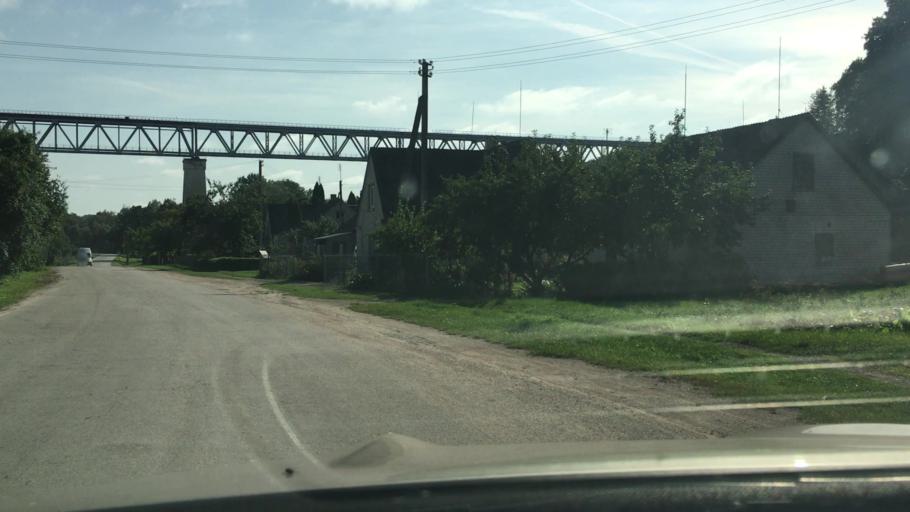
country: LT
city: Raseiniai
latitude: 55.5073
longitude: 23.0827
